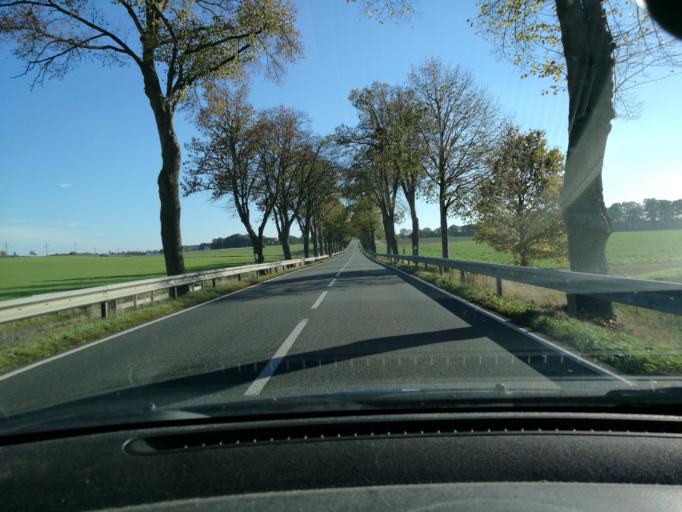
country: DE
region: Lower Saxony
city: Nahrendorf
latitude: 53.1664
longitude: 10.7907
